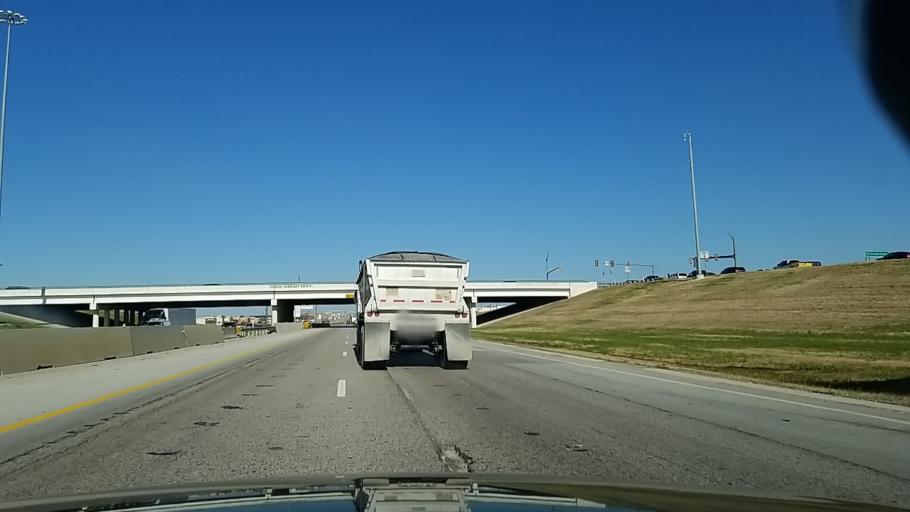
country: US
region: Texas
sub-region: Tarrant County
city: Blue Mound
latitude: 32.8971
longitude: -97.3171
